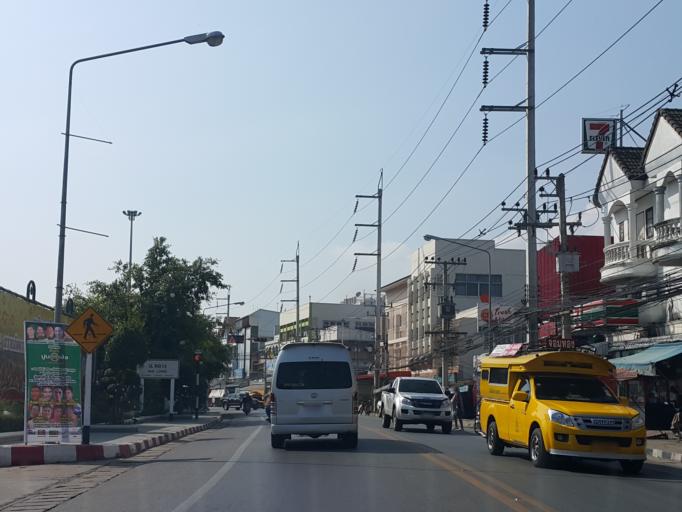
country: TH
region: Chiang Mai
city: Chom Thong
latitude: 18.4213
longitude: 98.6783
